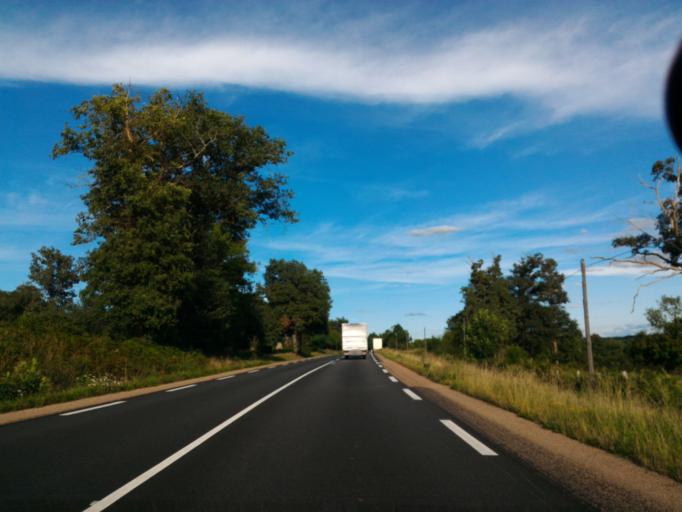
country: FR
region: Limousin
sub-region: Departement de la Haute-Vienne
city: Le Dorat
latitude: 46.1531
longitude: 1.1196
